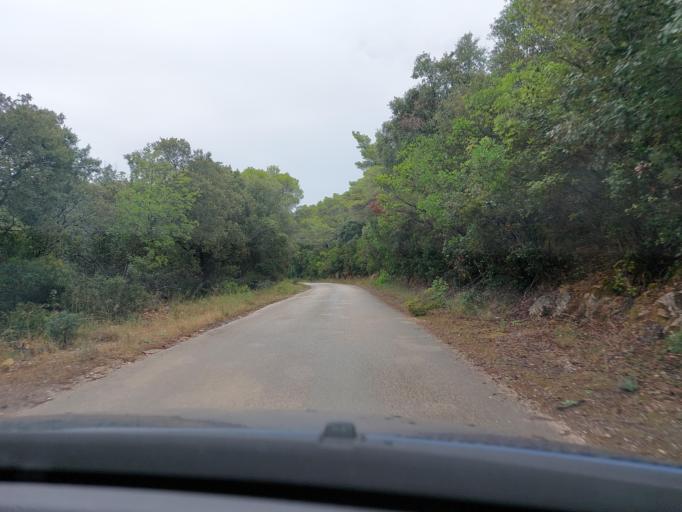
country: HR
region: Dubrovacko-Neretvanska
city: Smokvica
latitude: 42.7444
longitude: 16.8323
